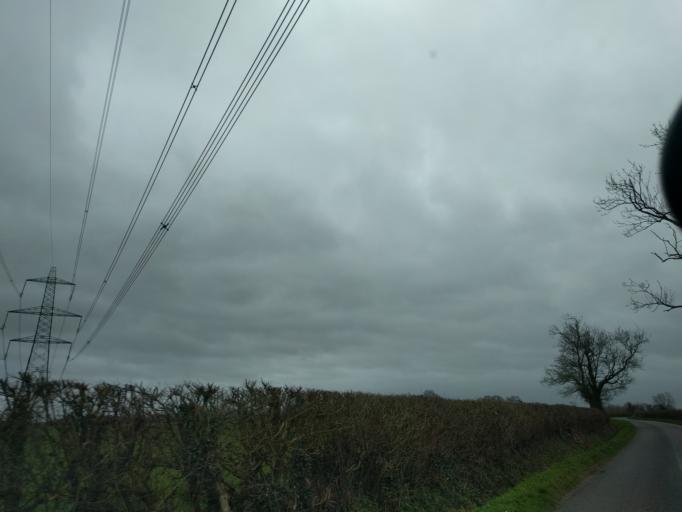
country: GB
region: England
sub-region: Wiltshire
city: Biddestone
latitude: 51.4765
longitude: -2.1961
